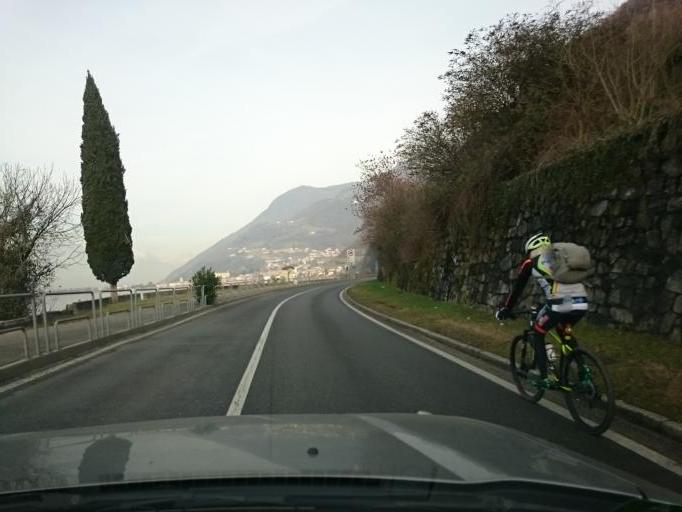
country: IT
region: Lombardy
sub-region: Provincia di Brescia
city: Pisogne
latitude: 45.7901
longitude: 10.0921
